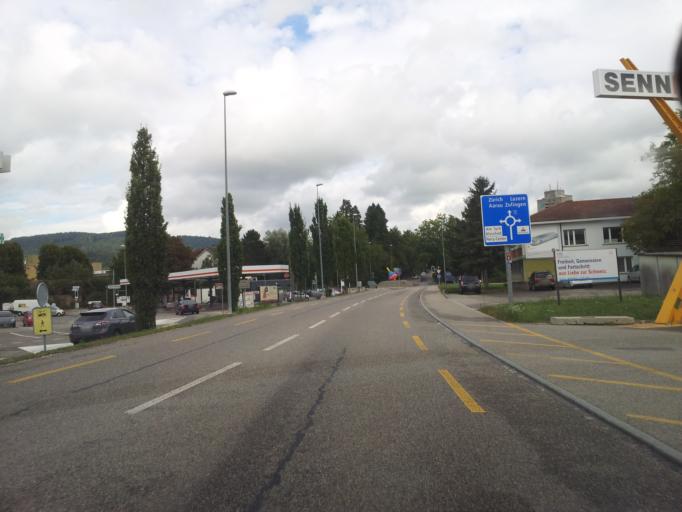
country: CH
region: Aargau
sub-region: Bezirk Zofingen
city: Oftringen
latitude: 47.3114
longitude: 7.9142
